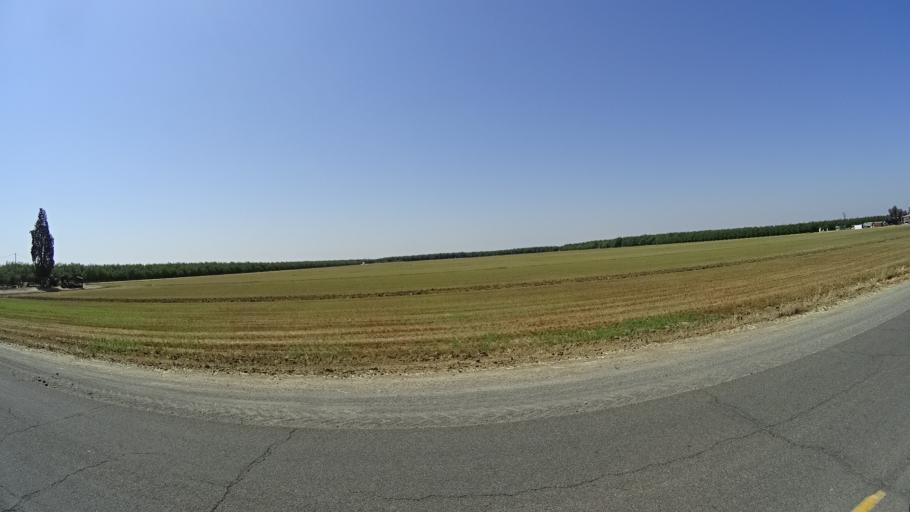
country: US
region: California
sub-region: Kings County
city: Hanford
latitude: 36.3717
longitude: -119.6023
